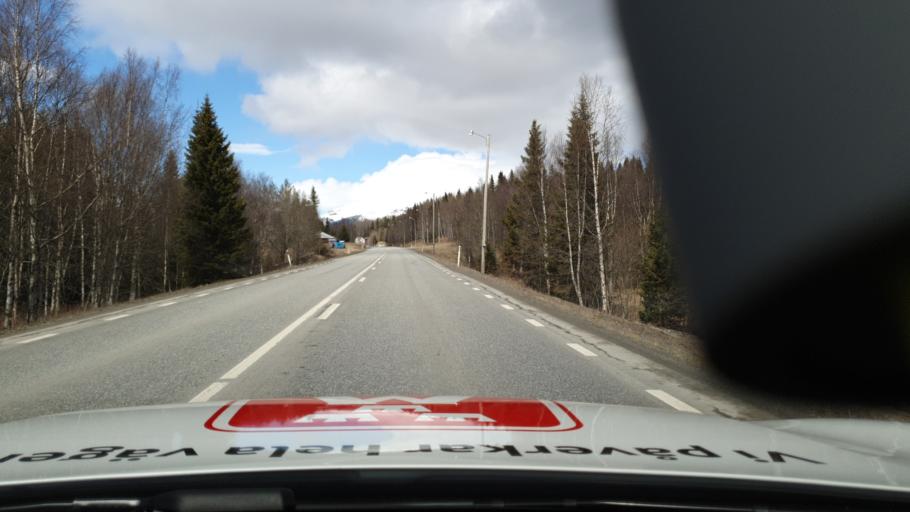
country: SE
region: Jaemtland
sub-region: Are Kommun
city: Are
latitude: 63.3357
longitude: 13.2132
